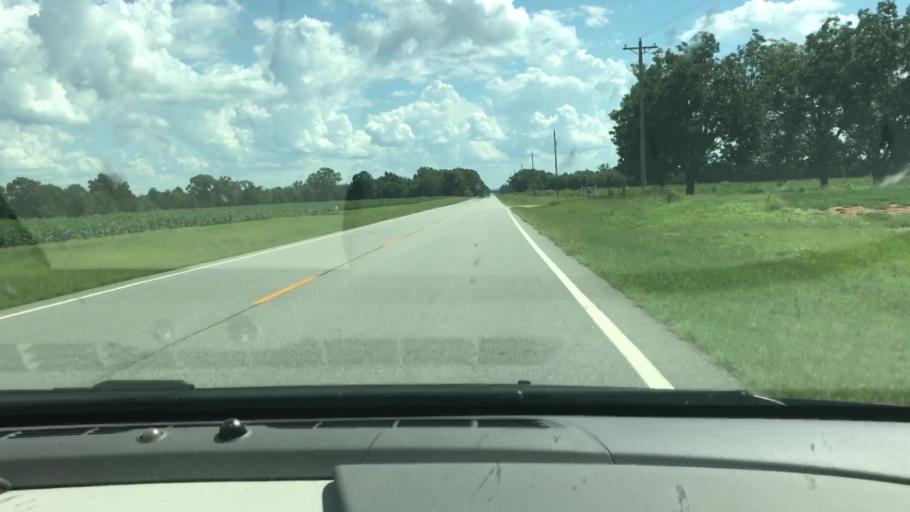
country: US
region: Georgia
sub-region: Quitman County
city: Georgetown
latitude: 31.8064
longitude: -85.0932
